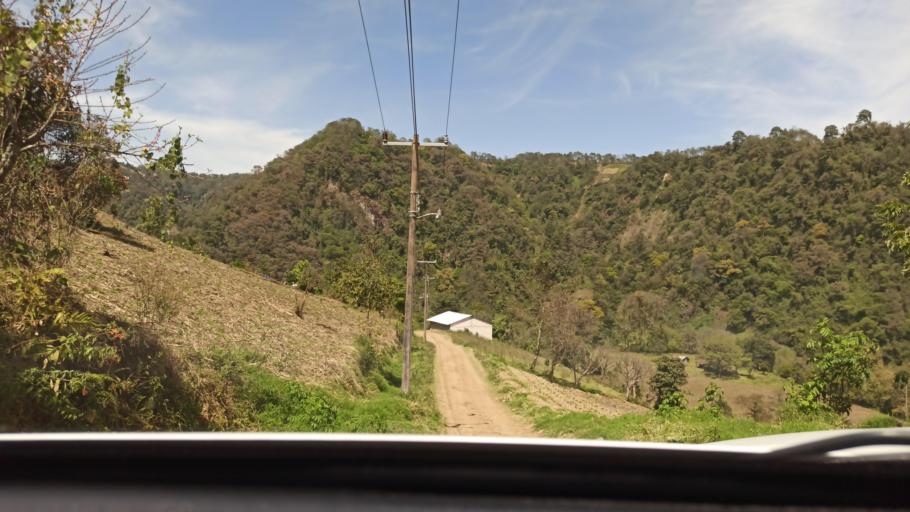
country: MX
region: Veracruz
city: Xocotla
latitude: 18.9911
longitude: -97.1001
